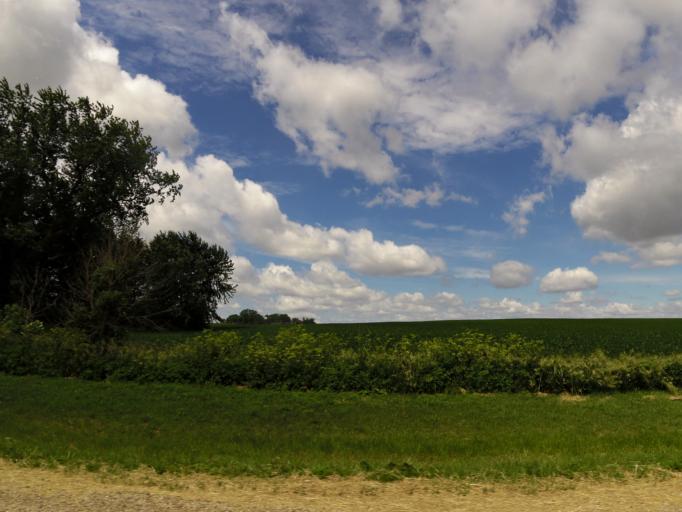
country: US
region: Iowa
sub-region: Chickasaw County
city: New Hampton
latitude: 43.1715
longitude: -92.2987
